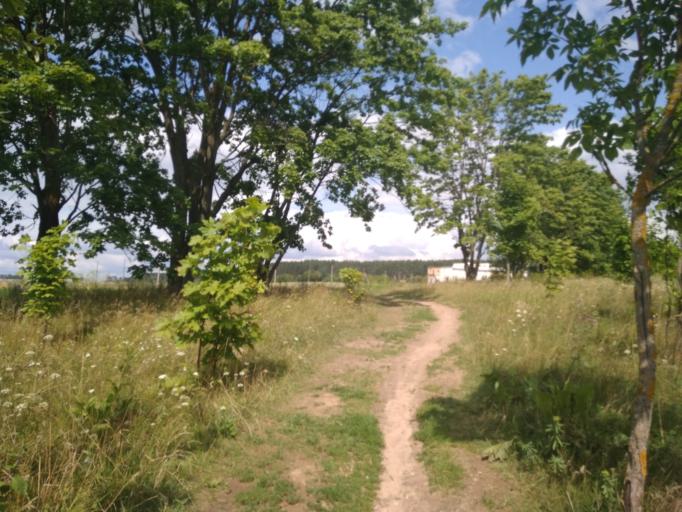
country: BY
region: Minsk
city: Minsk
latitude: 53.9442
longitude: 27.5657
